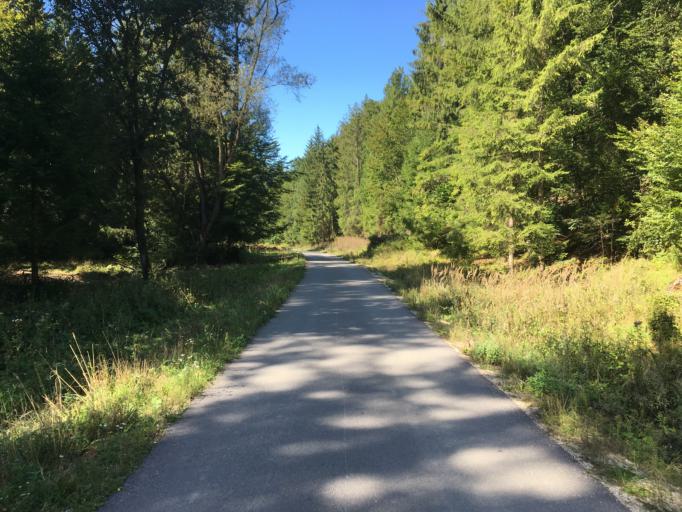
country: SK
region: Trenciansky
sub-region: Okres Povazska Bystrica
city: Povazska Bystrica
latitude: 49.0077
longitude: 18.4551
